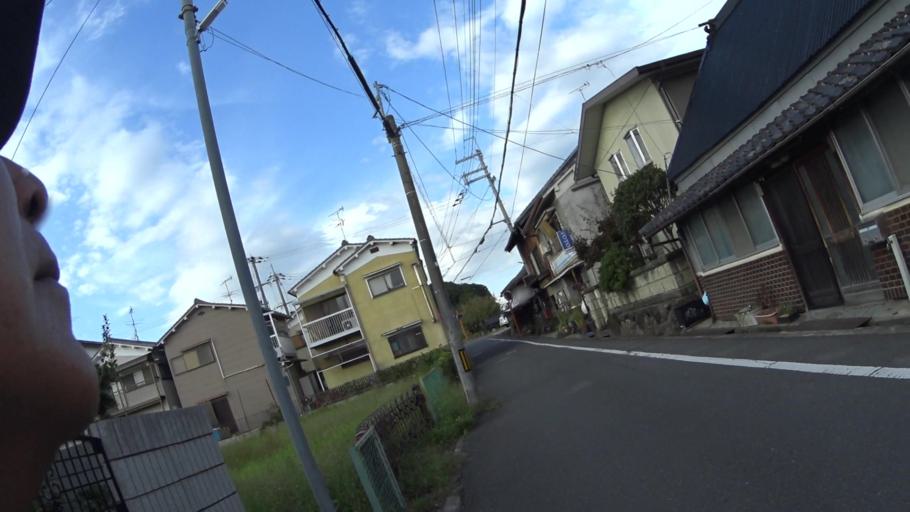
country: JP
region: Nara
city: Sakurai
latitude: 34.5363
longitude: 135.8417
